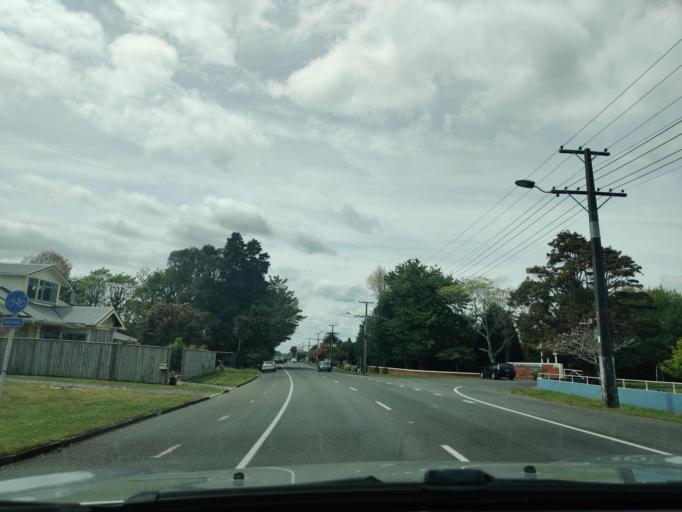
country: NZ
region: Taranaki
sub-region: New Plymouth District
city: New Plymouth
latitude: -39.1539
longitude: 174.1907
